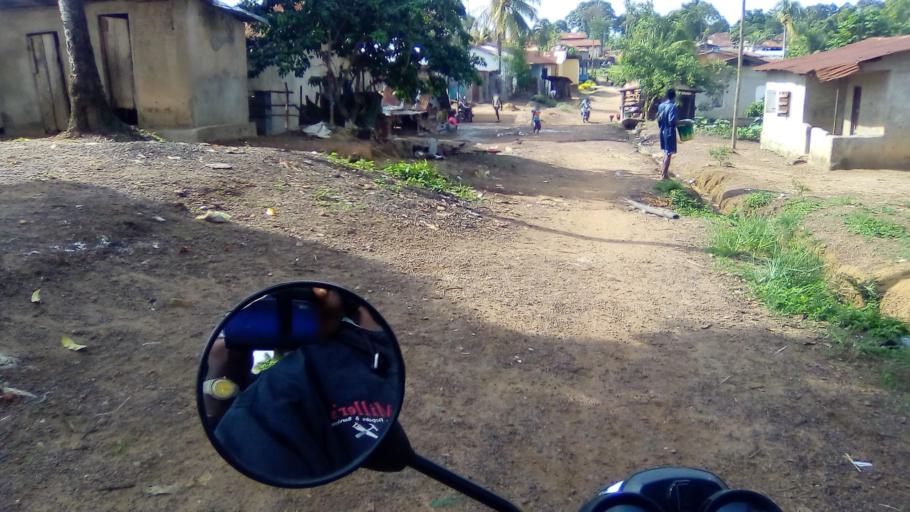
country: SL
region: Southern Province
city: Bo
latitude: 7.9582
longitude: -11.7578
